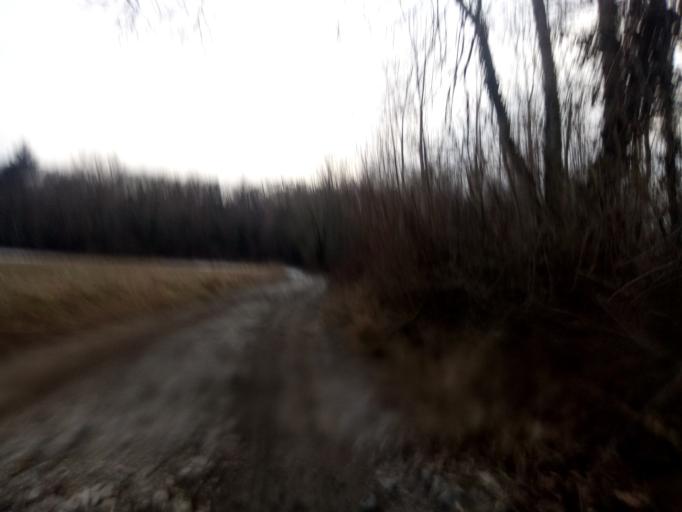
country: IT
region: Piedmont
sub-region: Provincia di Torino
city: Cascinette d'Ivrea
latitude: 45.4817
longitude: 7.9006
